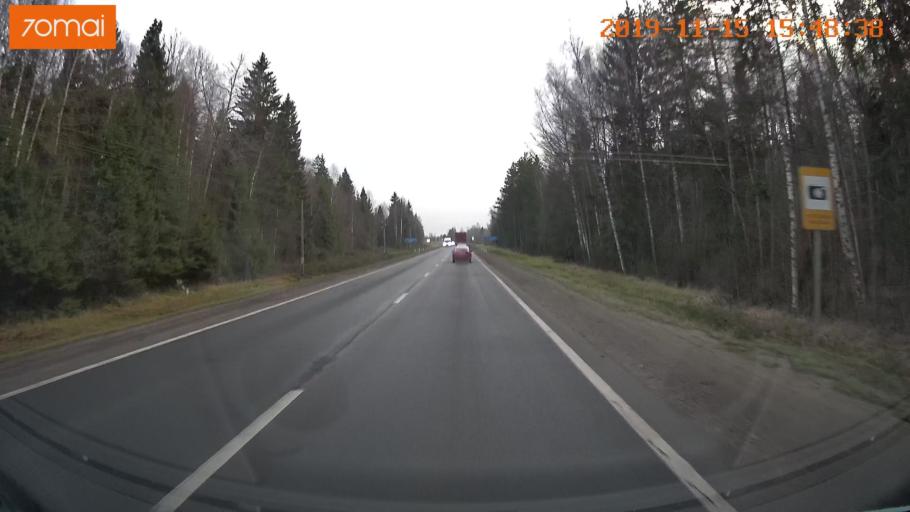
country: RU
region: Jaroslavl
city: Danilov
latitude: 57.9251
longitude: 40.0066
